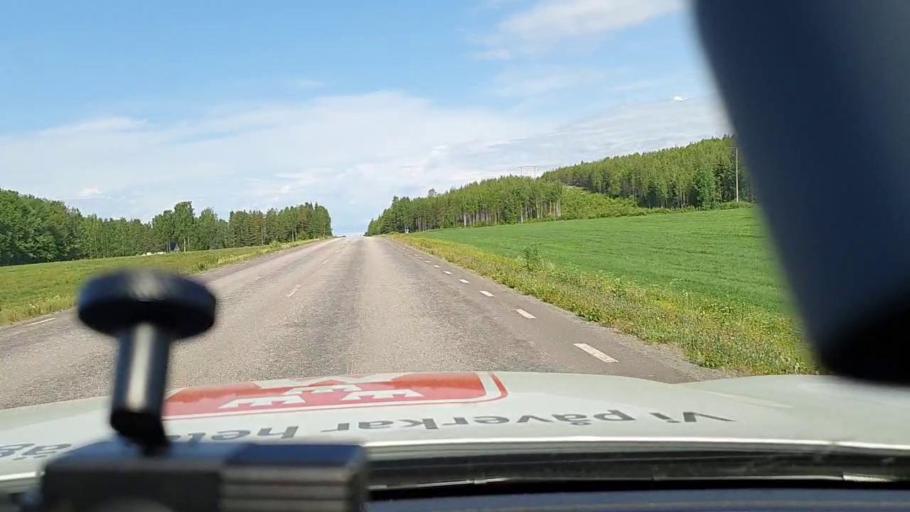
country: SE
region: Norrbotten
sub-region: Bodens Kommun
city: Boden
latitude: 65.9134
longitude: 21.3428
